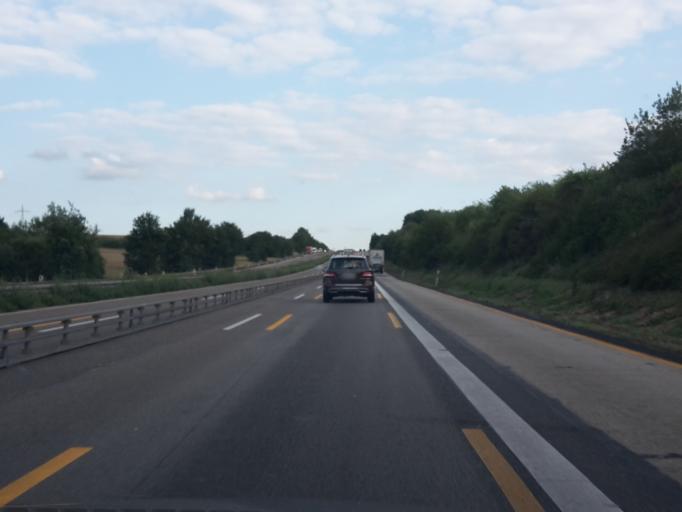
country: DE
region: Hesse
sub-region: Regierungsbezirk Giessen
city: Villmar
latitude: 50.3506
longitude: 8.1639
